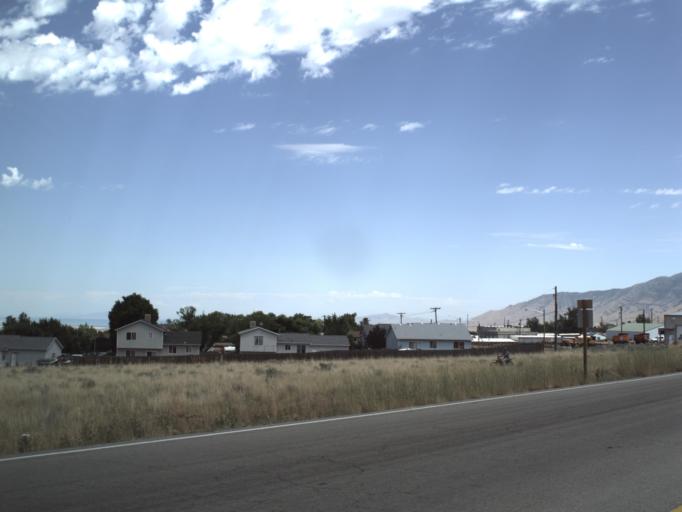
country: US
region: Utah
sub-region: Tooele County
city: Tooele
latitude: 40.5073
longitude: -112.3177
